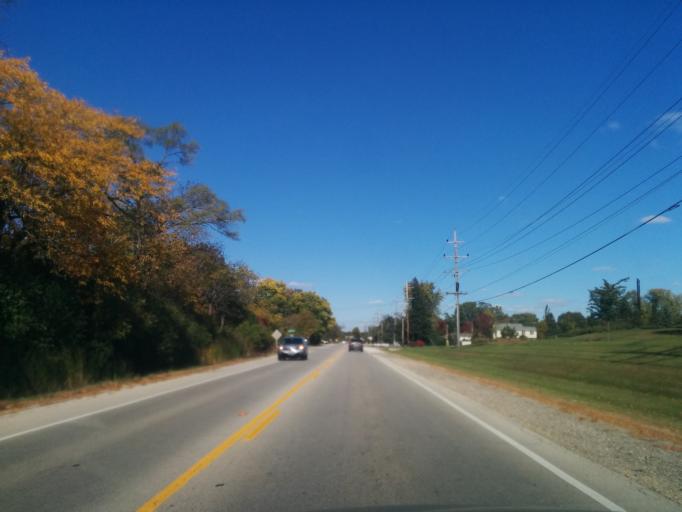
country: US
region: Illinois
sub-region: DuPage County
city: Lombard
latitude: 41.8690
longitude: -88.0331
